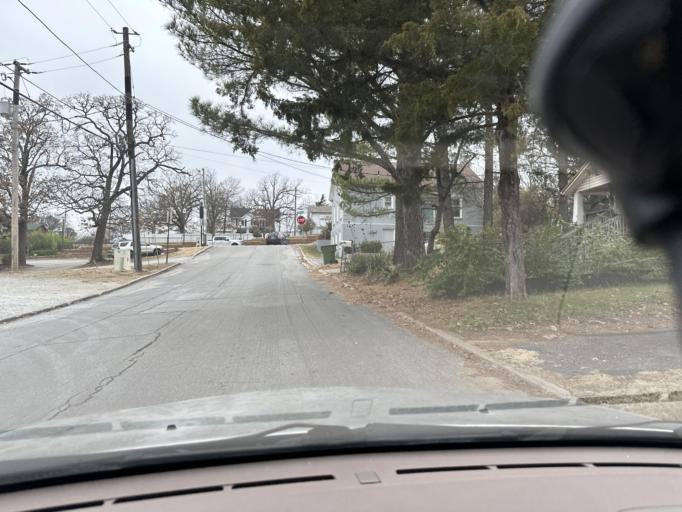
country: US
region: Arkansas
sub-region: Washington County
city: Fayetteville
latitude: 36.0741
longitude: -94.1567
